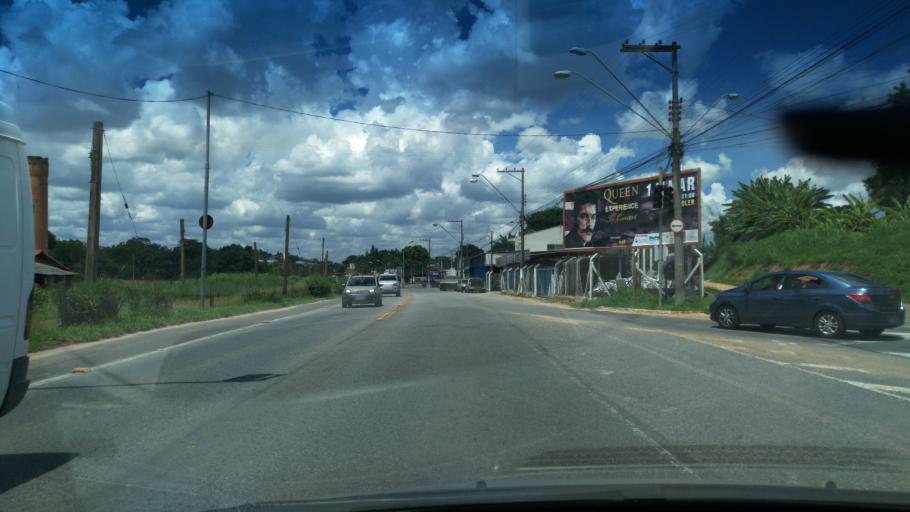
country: BR
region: Sao Paulo
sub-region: Vinhedo
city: Vinhedo
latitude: -23.0034
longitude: -46.9882
